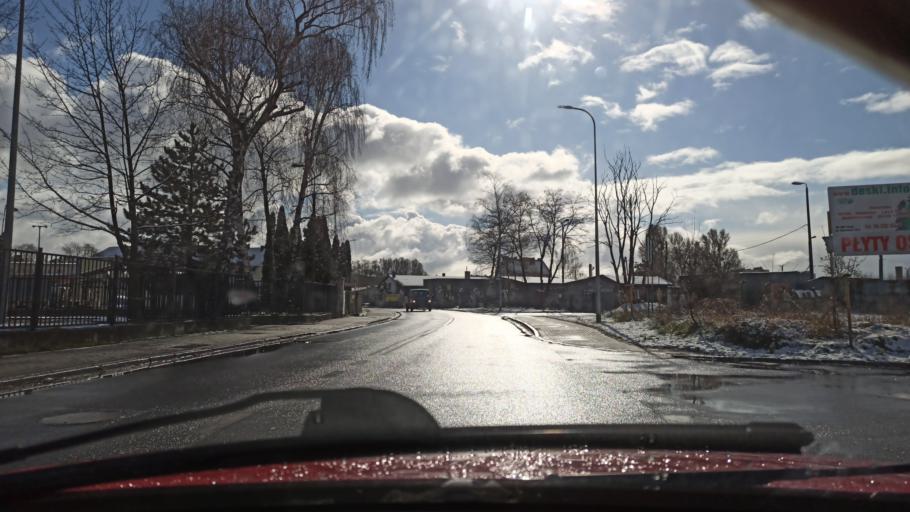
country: PL
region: Warmian-Masurian Voivodeship
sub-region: Powiat elblaski
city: Elblag
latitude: 54.1530
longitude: 19.3973
